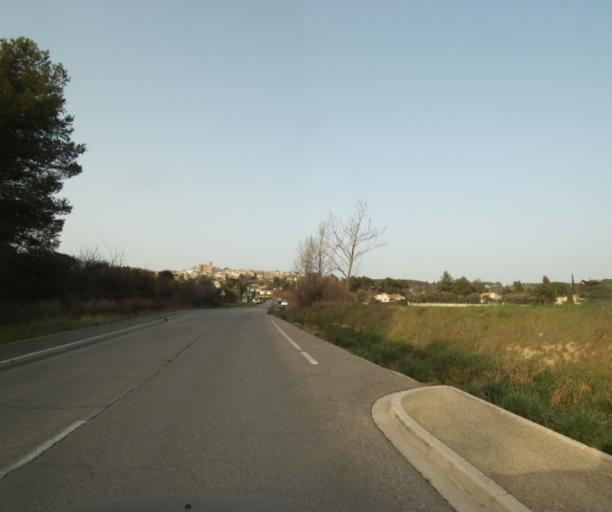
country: FR
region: Provence-Alpes-Cote d'Azur
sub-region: Departement des Bouches-du-Rhone
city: Eguilles
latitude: 43.5610
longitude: 5.3529
